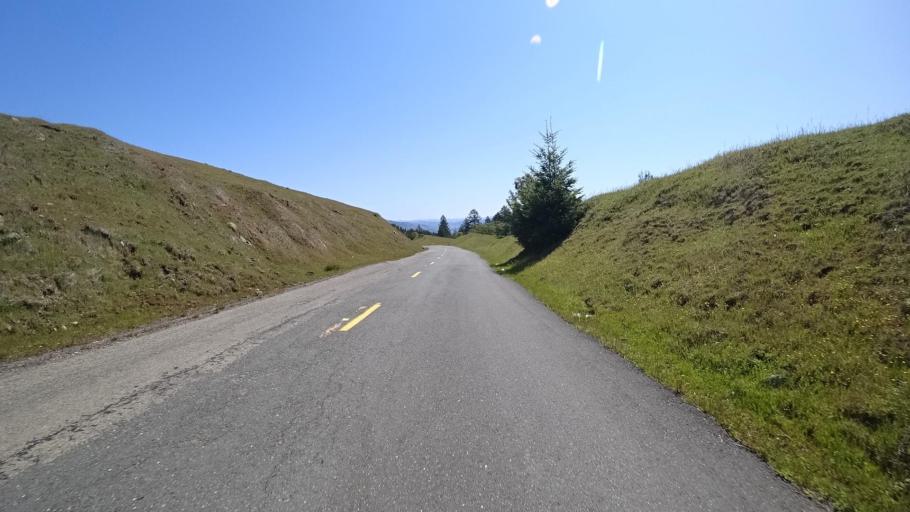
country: US
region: California
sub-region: Humboldt County
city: Redway
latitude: 40.1223
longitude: -123.6585
